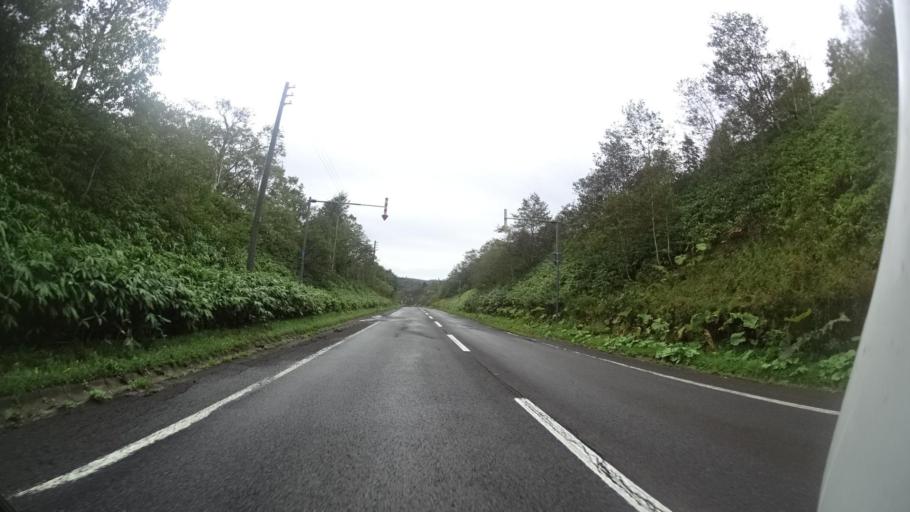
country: JP
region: Hokkaido
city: Shibetsu
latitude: 43.7577
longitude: 144.8068
